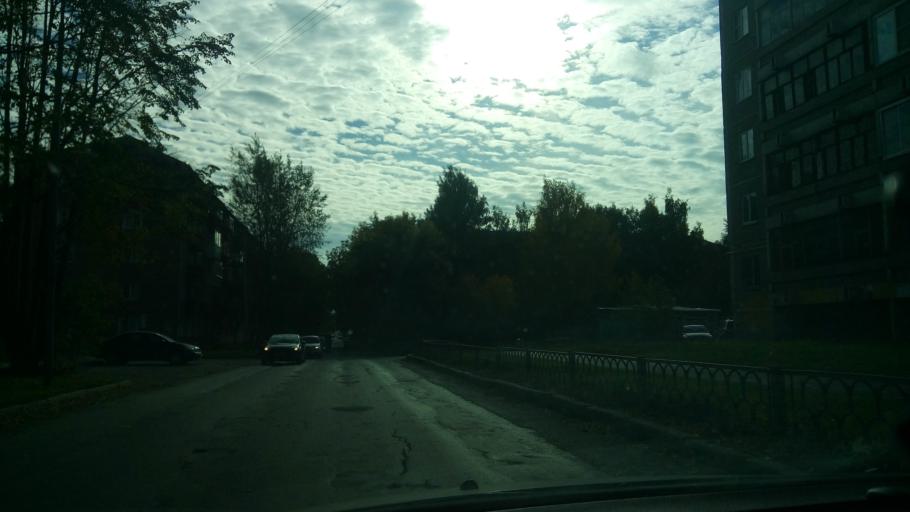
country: RU
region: Sverdlovsk
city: Yekaterinburg
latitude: 56.9020
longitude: 60.6021
